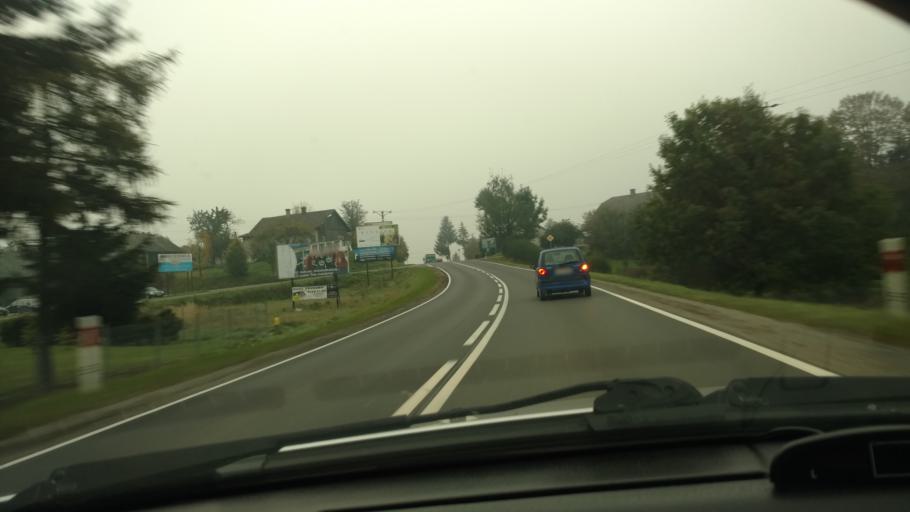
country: PL
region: Subcarpathian Voivodeship
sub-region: Powiat strzyzowski
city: Frysztak
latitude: 49.8324
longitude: 21.6147
